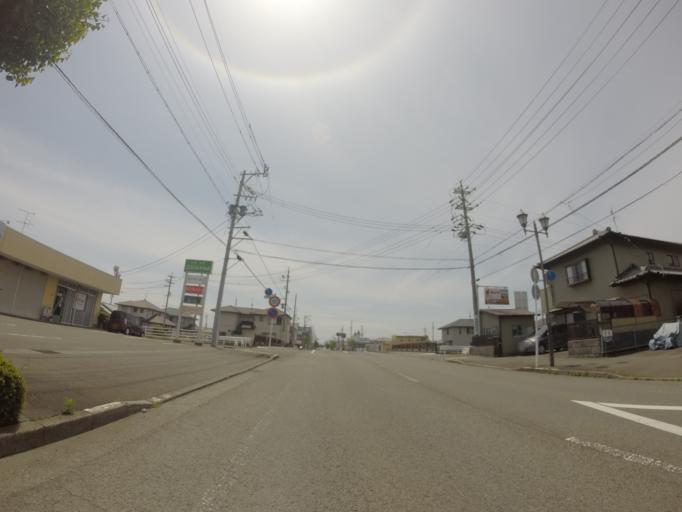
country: JP
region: Shizuoka
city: Yaizu
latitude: 34.8494
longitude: 138.3083
